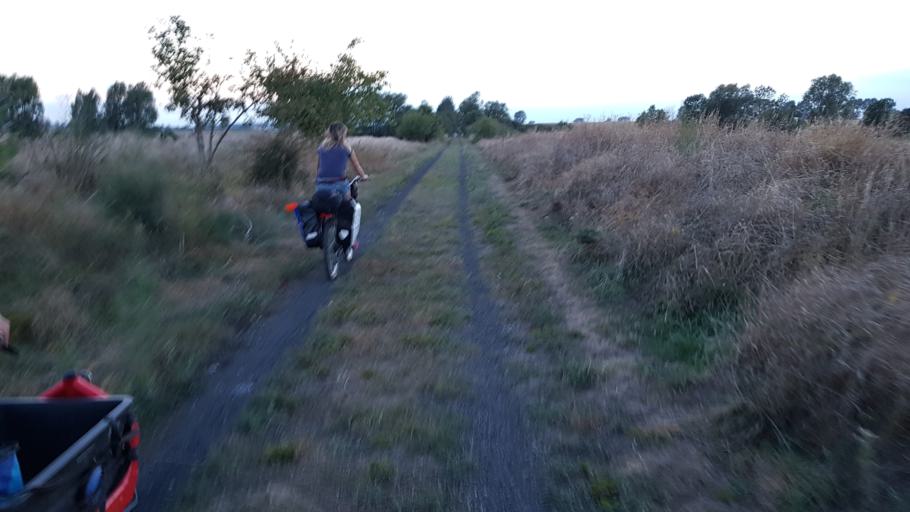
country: PL
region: West Pomeranian Voivodeship
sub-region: Powiat pyrzycki
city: Przelewice
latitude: 53.1310
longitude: 15.0365
